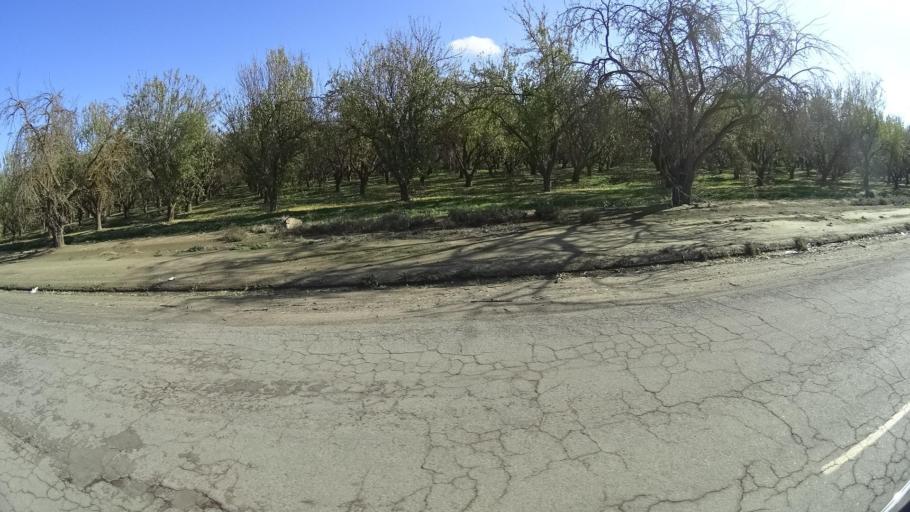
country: US
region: California
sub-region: Kern County
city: McFarland
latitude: 35.7013
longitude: -119.2586
